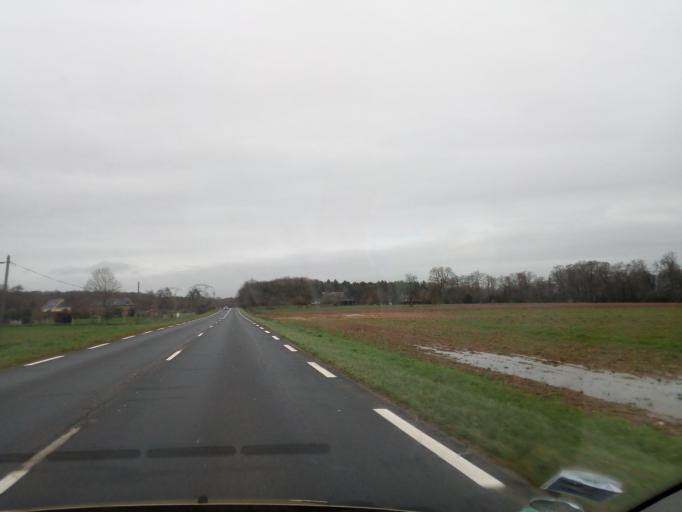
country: FR
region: Haute-Normandie
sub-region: Departement de l'Eure
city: Hauville
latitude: 49.4082
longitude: 0.7969
